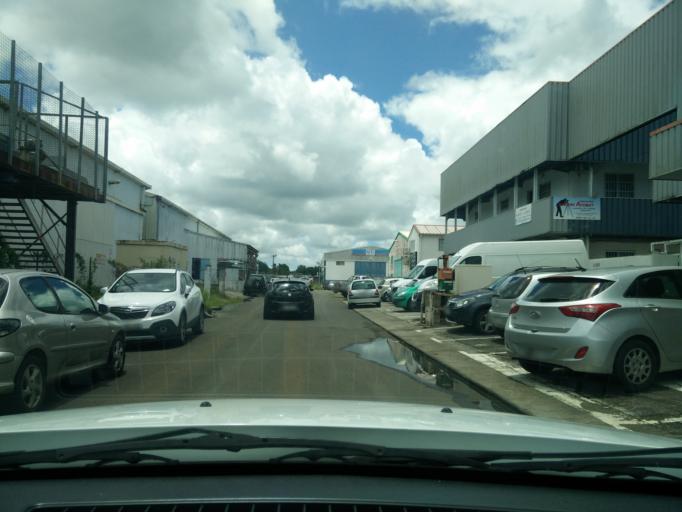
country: GP
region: Guadeloupe
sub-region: Guadeloupe
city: Les Abymes
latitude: 16.2578
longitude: -61.5097
